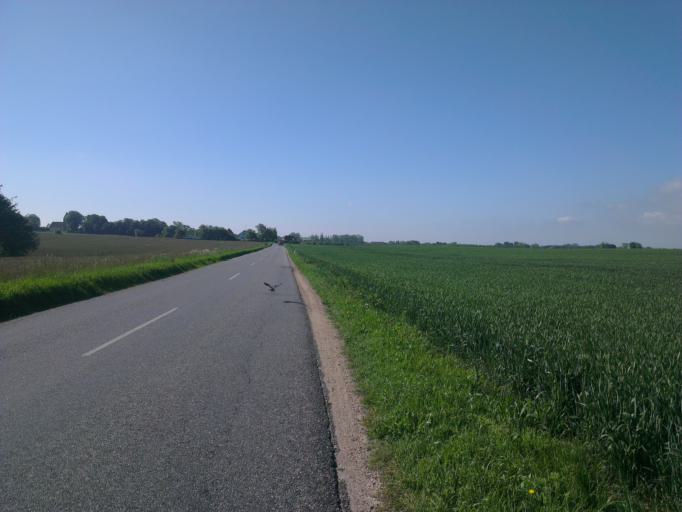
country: DK
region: Capital Region
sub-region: Frederikssund Kommune
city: Skibby
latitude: 55.7897
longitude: 12.0116
